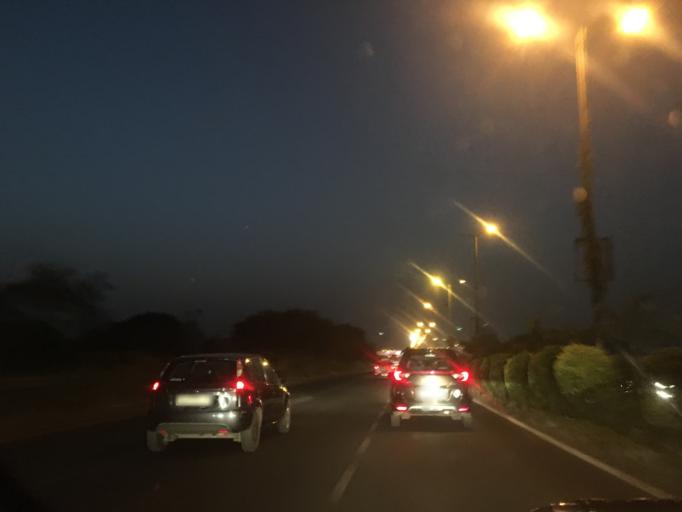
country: IN
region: Maharashtra
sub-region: Thane
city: Airoli
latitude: 19.1525
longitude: 72.9703
